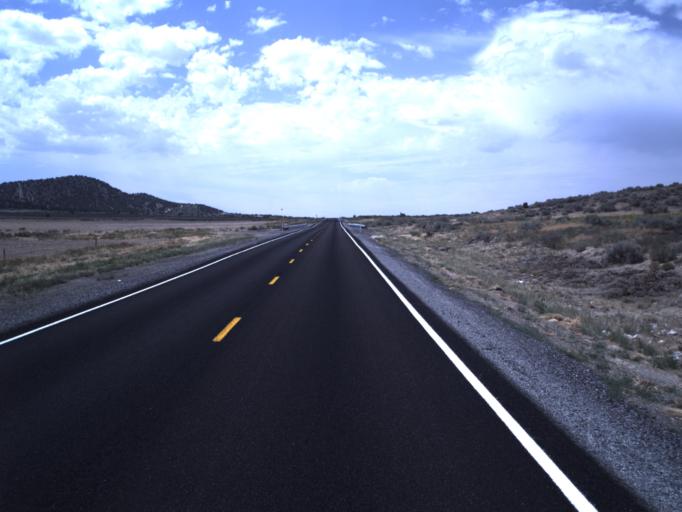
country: US
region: Utah
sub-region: Utah County
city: Eagle Mountain
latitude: 40.2397
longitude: -112.1532
